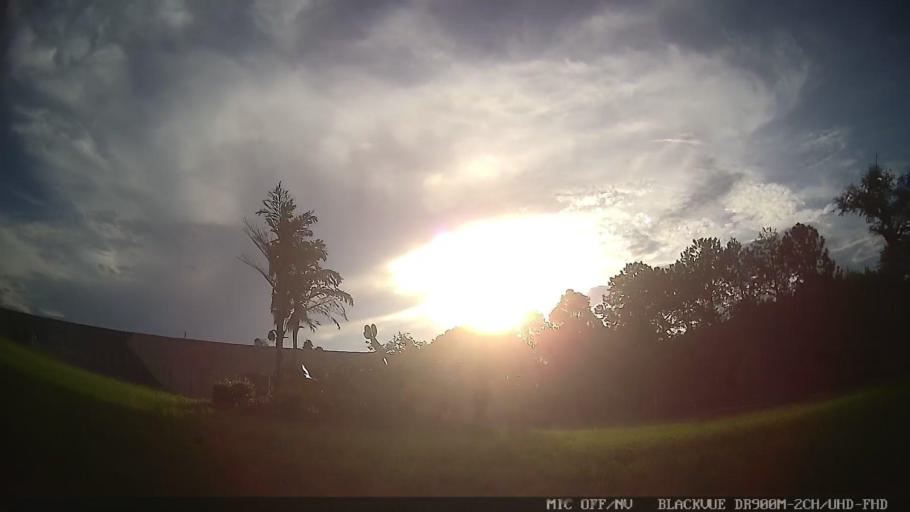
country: BR
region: Sao Paulo
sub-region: Cerquilho
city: Cerquilho
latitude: -23.1762
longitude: -47.6410
